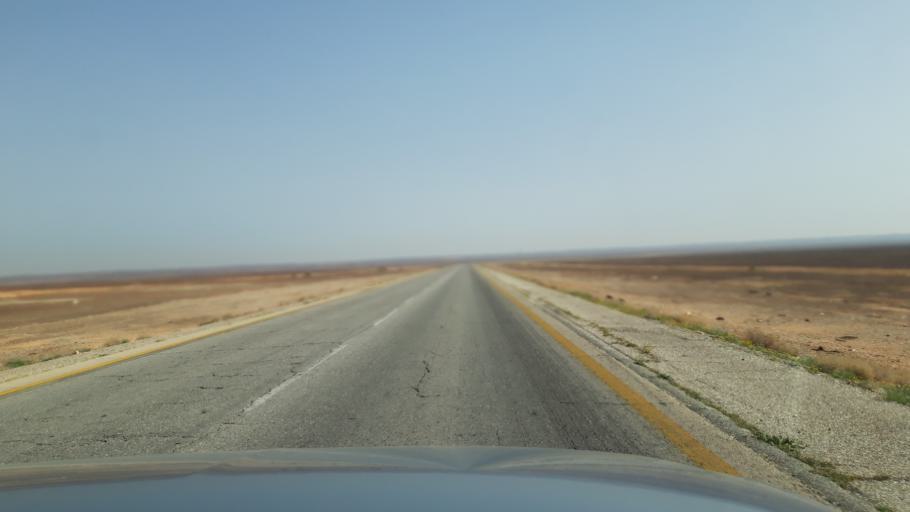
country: JO
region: Amman
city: Al Azraq ash Shamali
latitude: 31.8101
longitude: 36.5953
